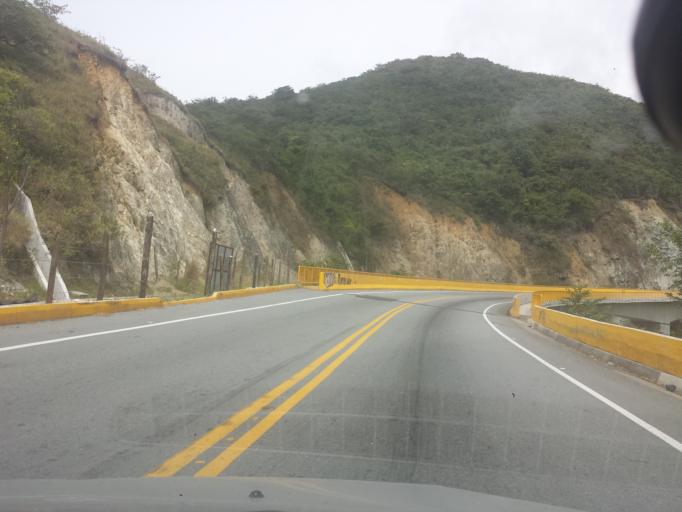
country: CO
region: Antioquia
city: Antioquia
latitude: 6.6122
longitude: -75.8479
